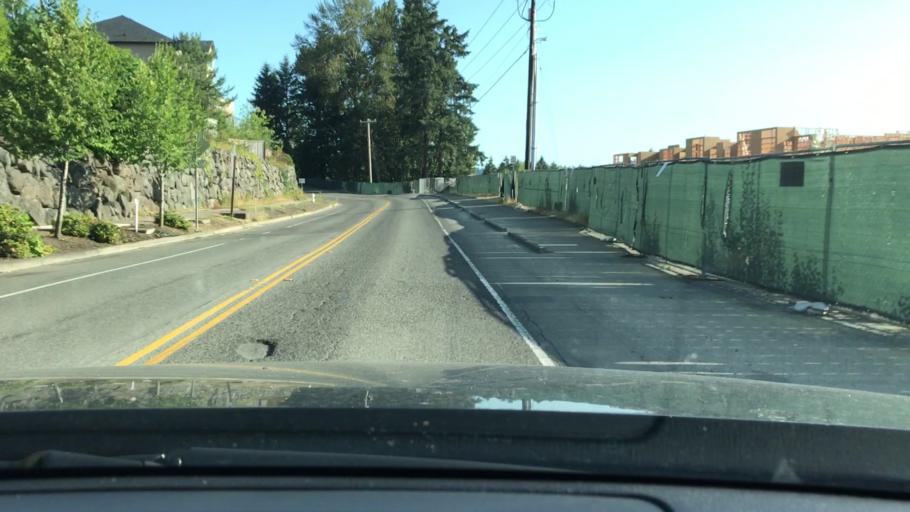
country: US
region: Washington
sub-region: King County
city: West Lake Sammamish
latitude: 47.5515
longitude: -122.0756
